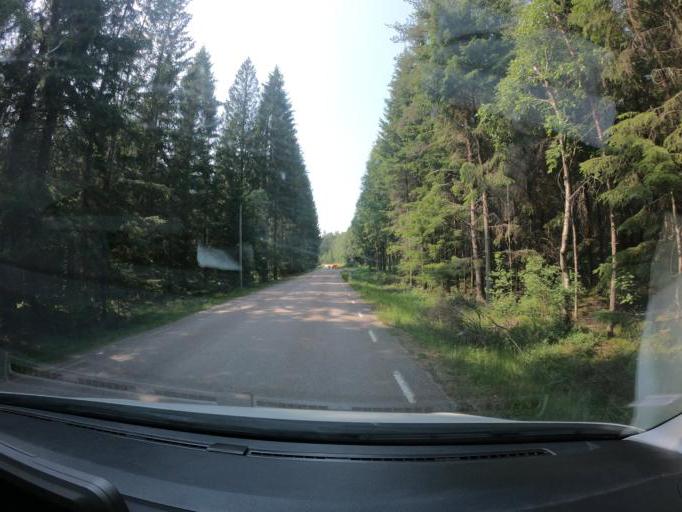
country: SE
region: Kronoberg
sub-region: Markaryds Kommun
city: Markaryd
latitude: 56.3336
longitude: 13.5704
